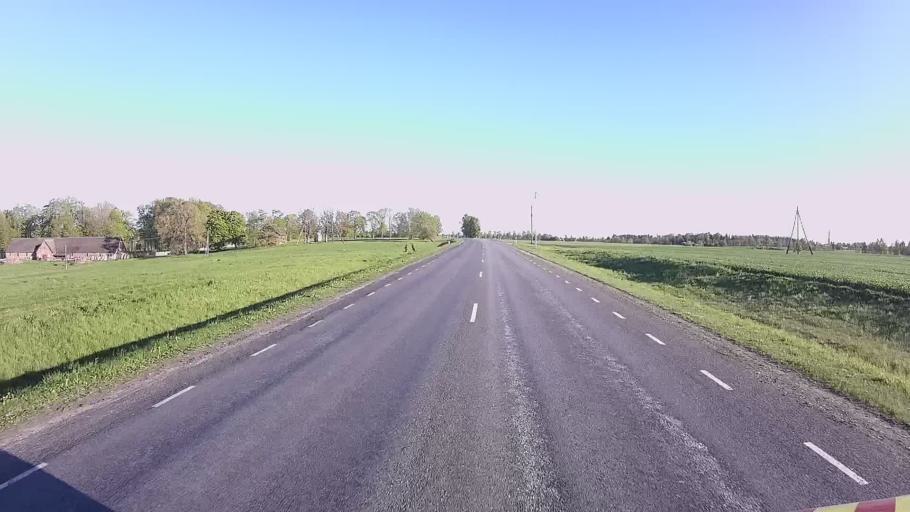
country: EE
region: Viljandimaa
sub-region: Viljandi linn
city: Viljandi
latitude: 58.3983
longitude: 25.5917
